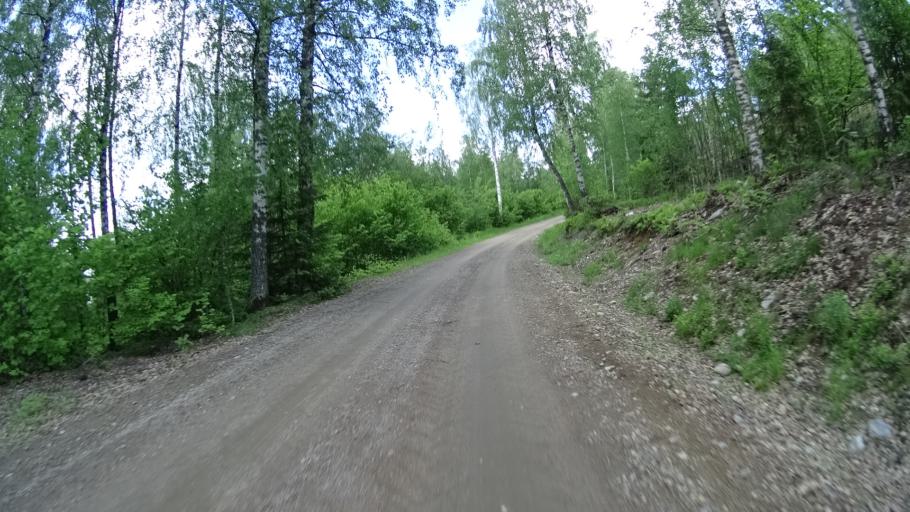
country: FI
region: Uusimaa
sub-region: Raaseporin
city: Karis
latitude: 60.1418
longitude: 23.6182
